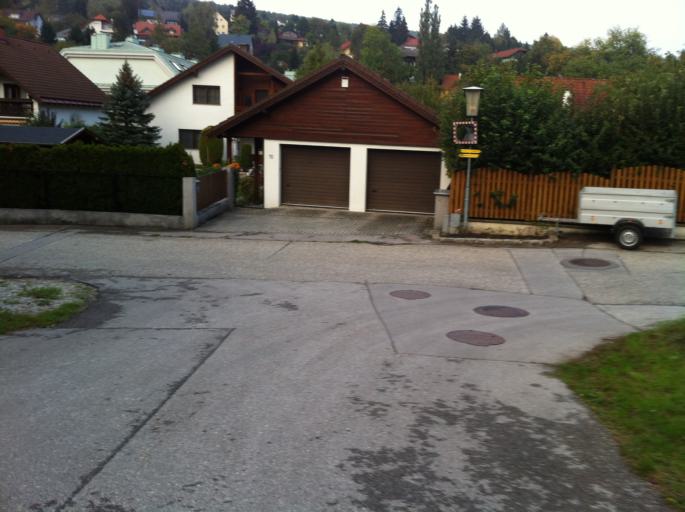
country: AT
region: Lower Austria
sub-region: Politischer Bezirk Wien-Umgebung
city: Gablitz
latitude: 48.2265
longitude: 16.1557
